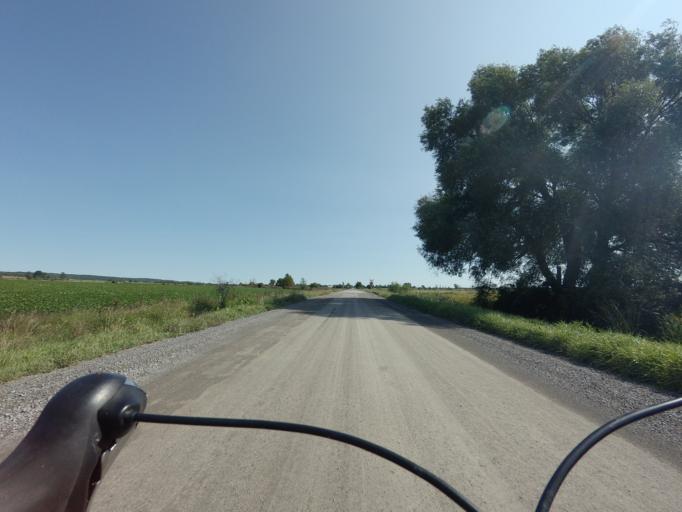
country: CA
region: Ontario
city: Arnprior
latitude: 45.3747
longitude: -76.1435
